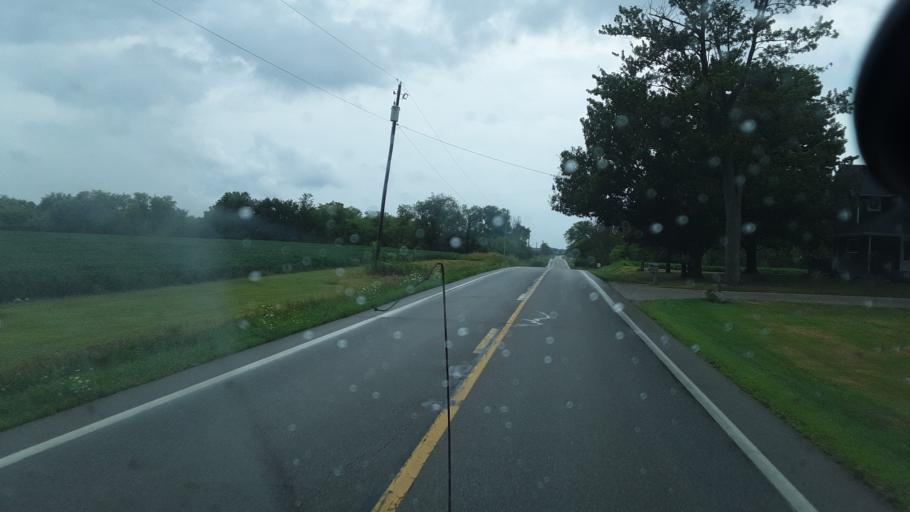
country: US
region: Ohio
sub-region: Williams County
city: Edgerton
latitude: 41.5564
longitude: -84.7912
